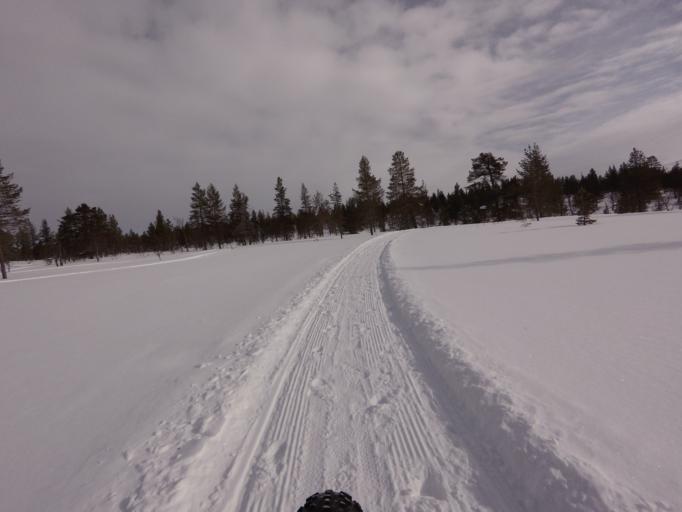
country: FI
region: Lapland
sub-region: Pohjois-Lappi
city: Ivalo
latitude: 68.3480
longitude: 27.4523
